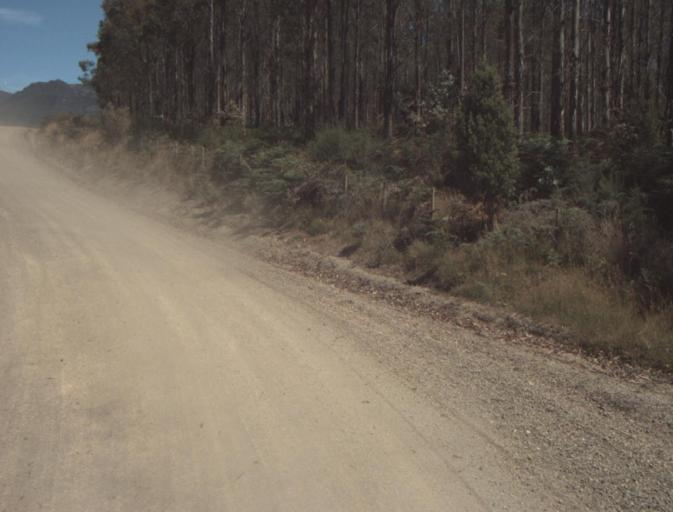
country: AU
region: Tasmania
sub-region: Dorset
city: Scottsdale
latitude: -41.3225
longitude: 147.4459
